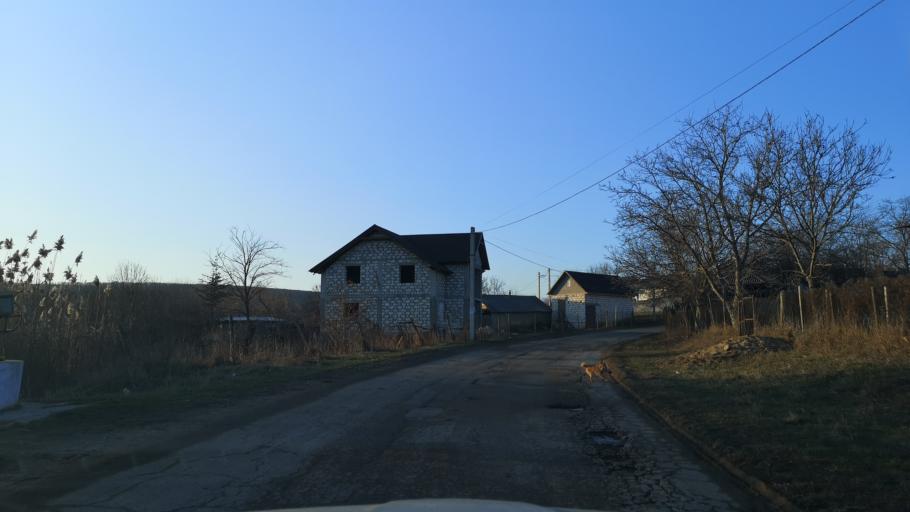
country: MD
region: Orhei
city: Orhei
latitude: 47.3552
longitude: 28.6904
